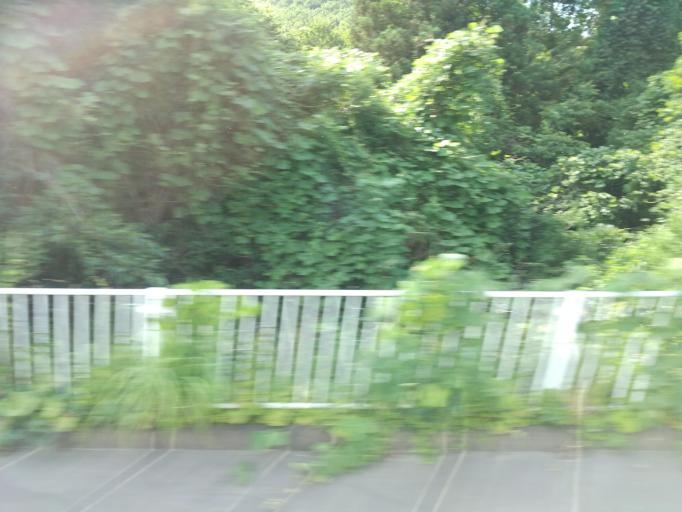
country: JP
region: Miyagi
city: Sendai
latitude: 38.2546
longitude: 140.7546
